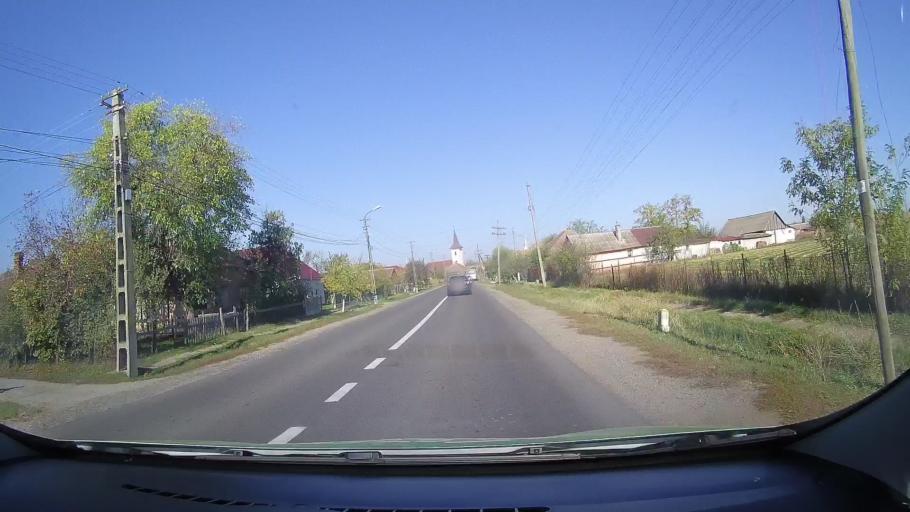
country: RO
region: Satu Mare
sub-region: Comuna Cauas
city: Cauas
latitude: 47.5661
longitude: 22.5469
